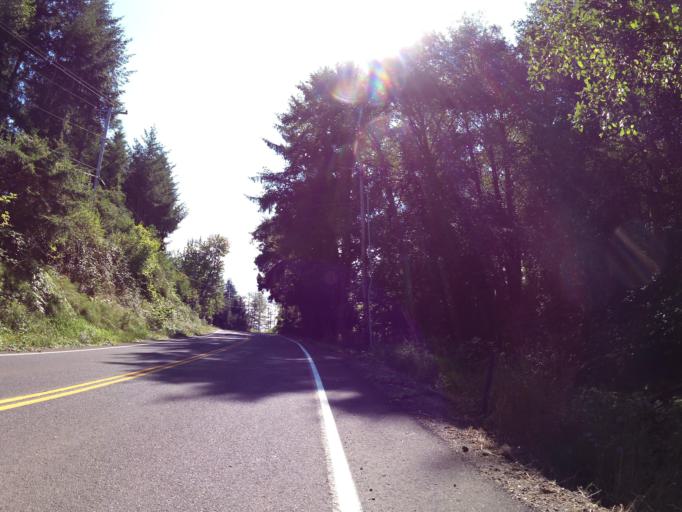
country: US
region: Washington
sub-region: Wahkiakum County
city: Cathlamet
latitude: 46.1810
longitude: -123.5835
